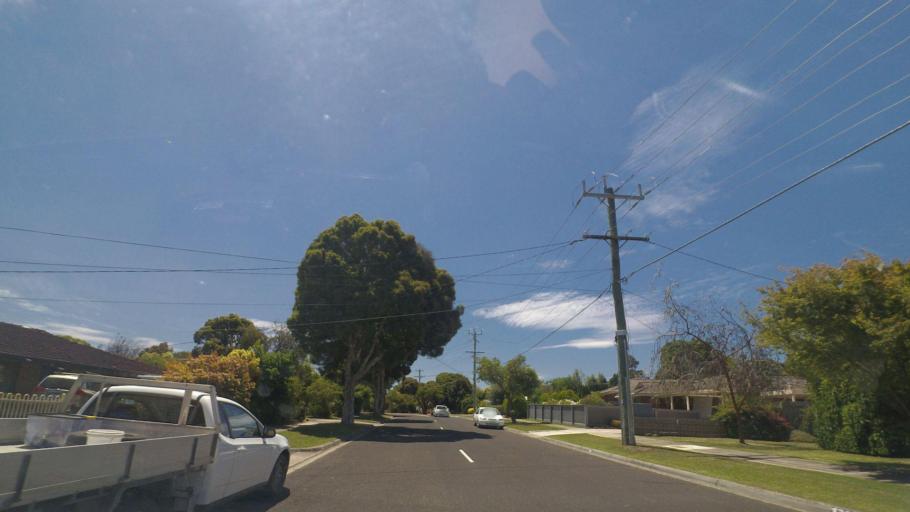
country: AU
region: Victoria
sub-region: Maroondah
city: Croydon North
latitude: -37.7721
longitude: 145.3210
